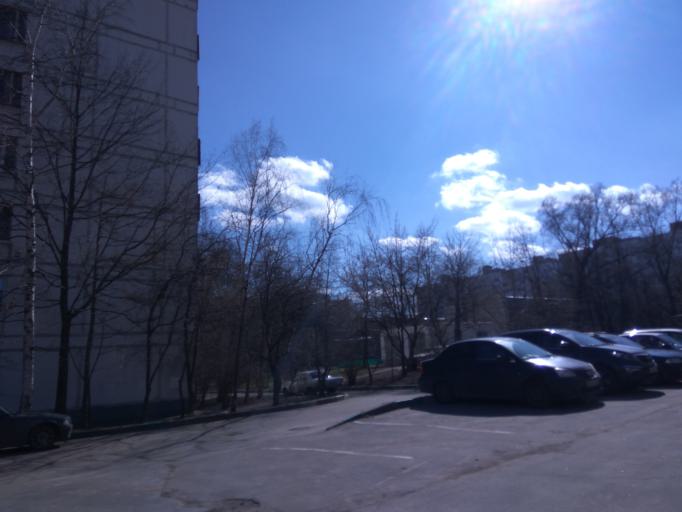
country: RU
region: Moscow
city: Ivanovskoye
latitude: 55.7817
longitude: 37.8344
